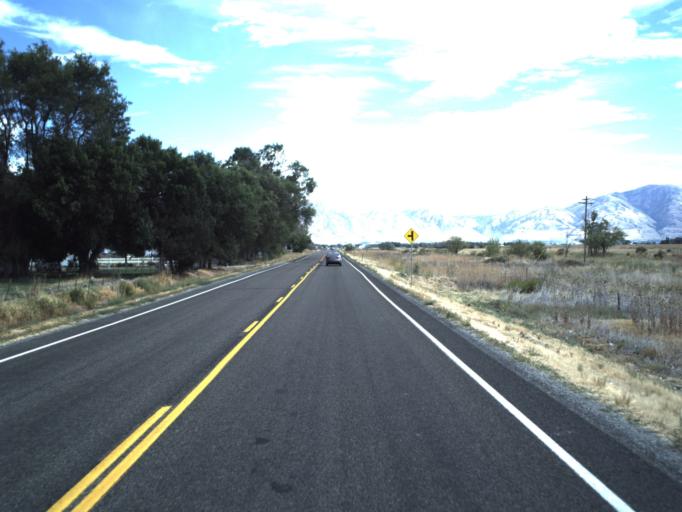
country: US
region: Utah
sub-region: Box Elder County
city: Honeyville
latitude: 41.5616
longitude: -112.1602
